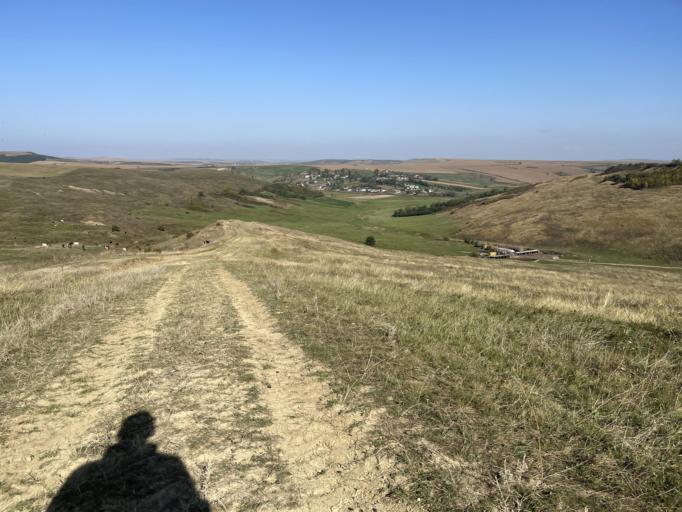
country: RO
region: Iasi
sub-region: Comuna Dumesti
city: Pausesti
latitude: 47.1516
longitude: 27.3106
